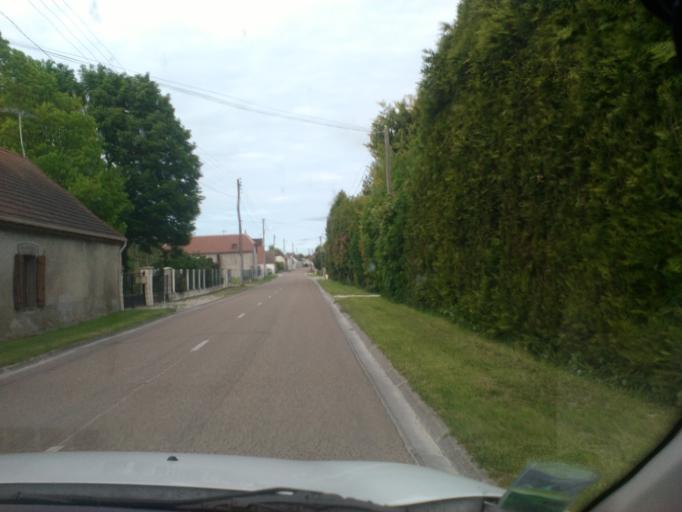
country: FR
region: Champagne-Ardenne
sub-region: Departement de l'Aube
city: Marigny-le-Chatel
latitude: 48.3581
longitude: 3.7059
